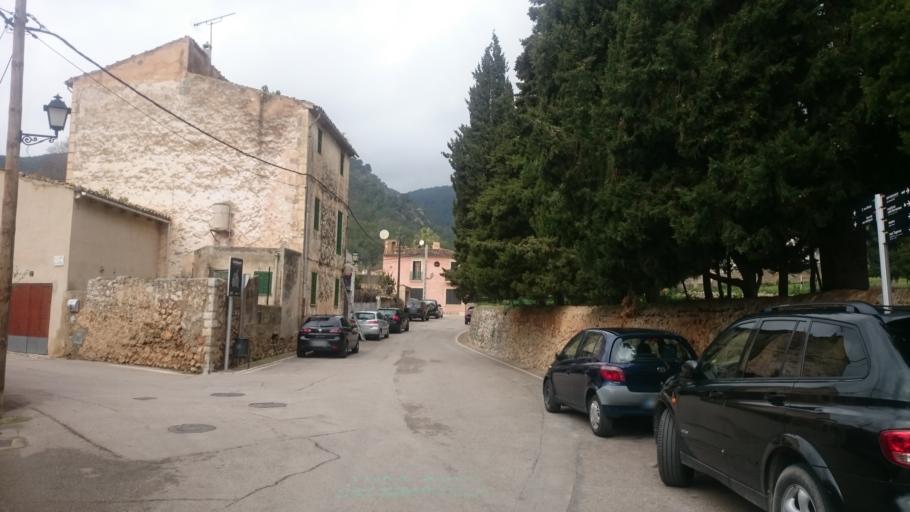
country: ES
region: Balearic Islands
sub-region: Illes Balears
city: Alaro
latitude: 39.7071
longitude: 2.7850
